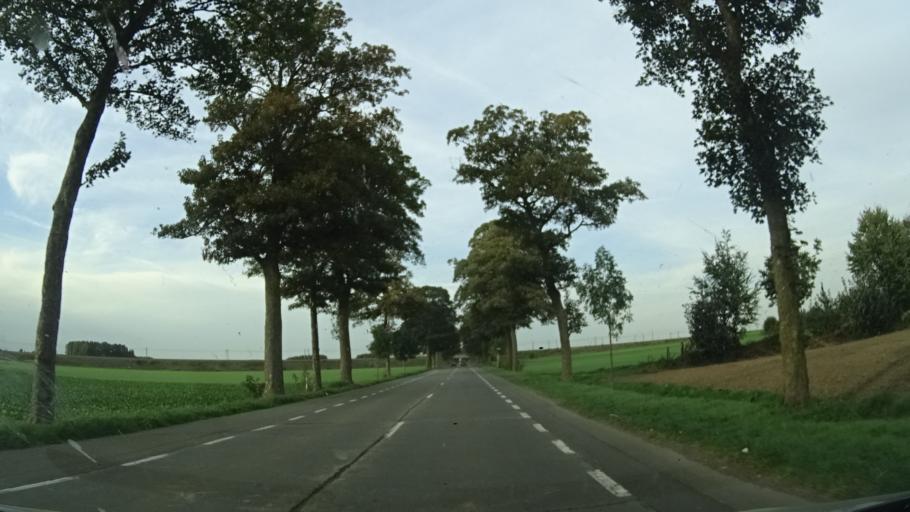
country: BE
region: Wallonia
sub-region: Province du Hainaut
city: Peruwelz
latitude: 50.5550
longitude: 3.6087
